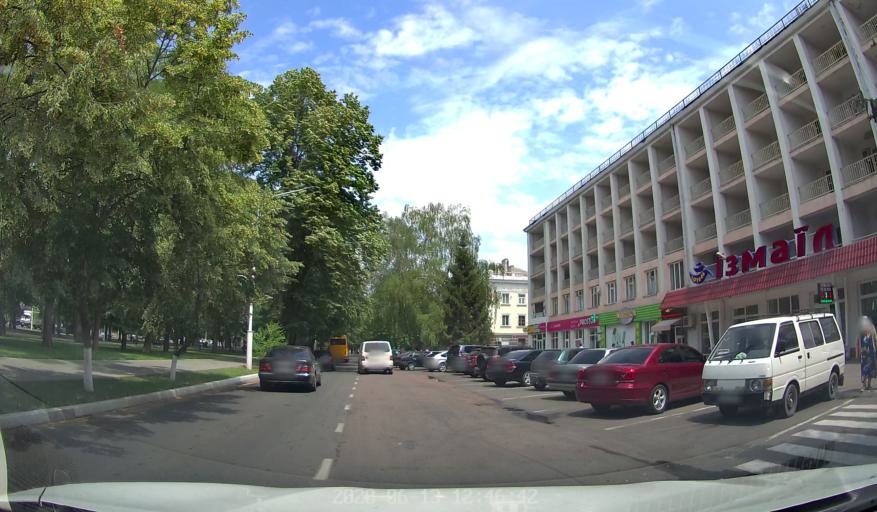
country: NE
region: Zinder
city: Kantche
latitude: 13.6034
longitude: 8.6497
